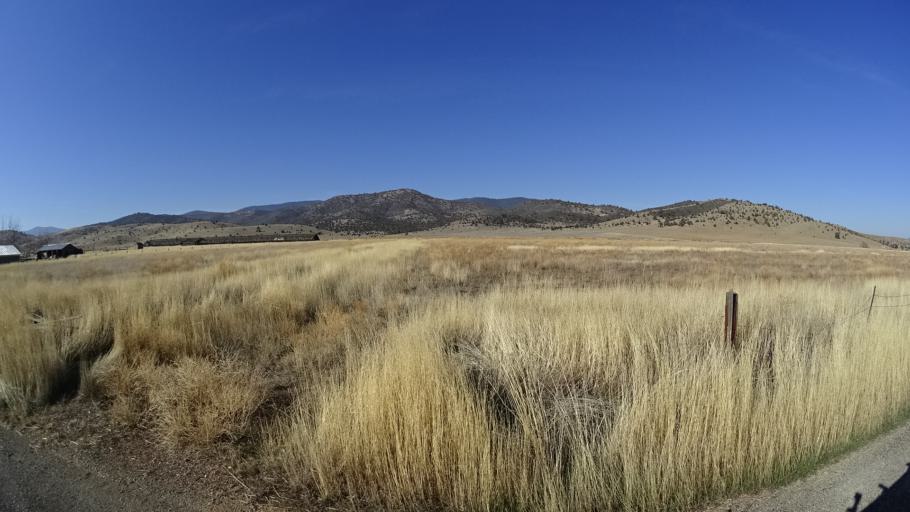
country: US
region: California
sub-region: Siskiyou County
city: Montague
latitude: 41.6198
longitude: -122.5298
